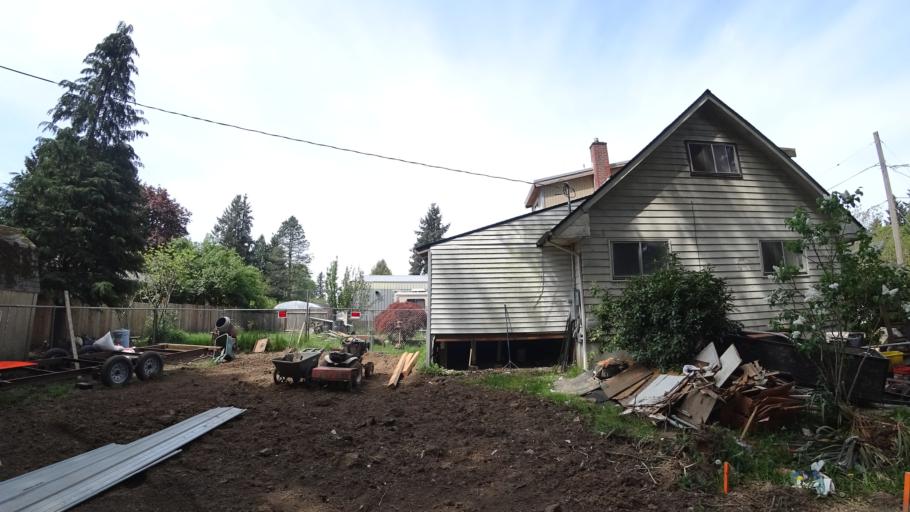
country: US
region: Oregon
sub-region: Clackamas County
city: Milwaukie
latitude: 45.4510
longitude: -122.6027
